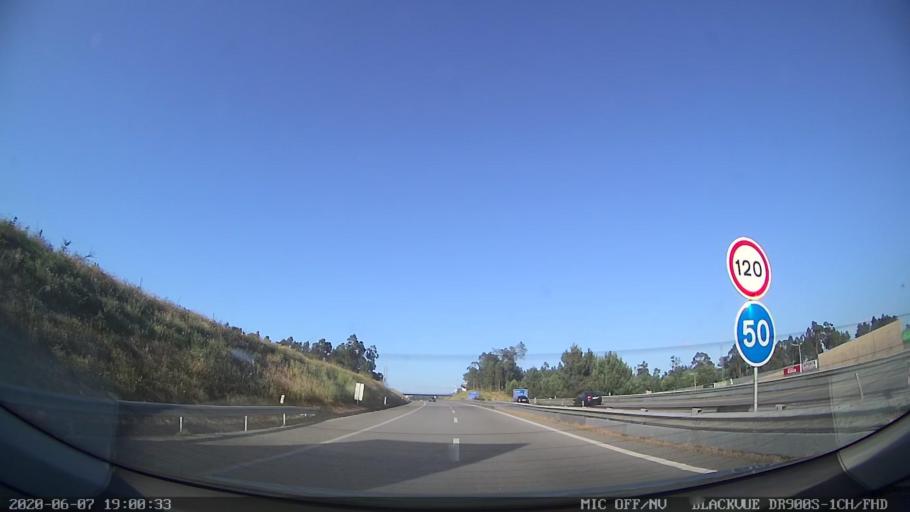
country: PT
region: Braga
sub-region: Vila Nova de Famalicao
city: Vila Nova de Famalicao
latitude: 41.3820
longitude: -8.4969
